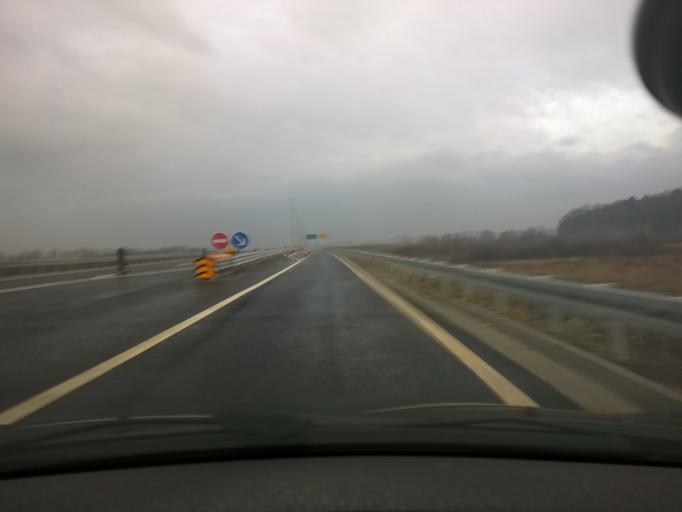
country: HR
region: Krapinsko-Zagorska
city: Zabok
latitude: 46.0135
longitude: 15.9432
